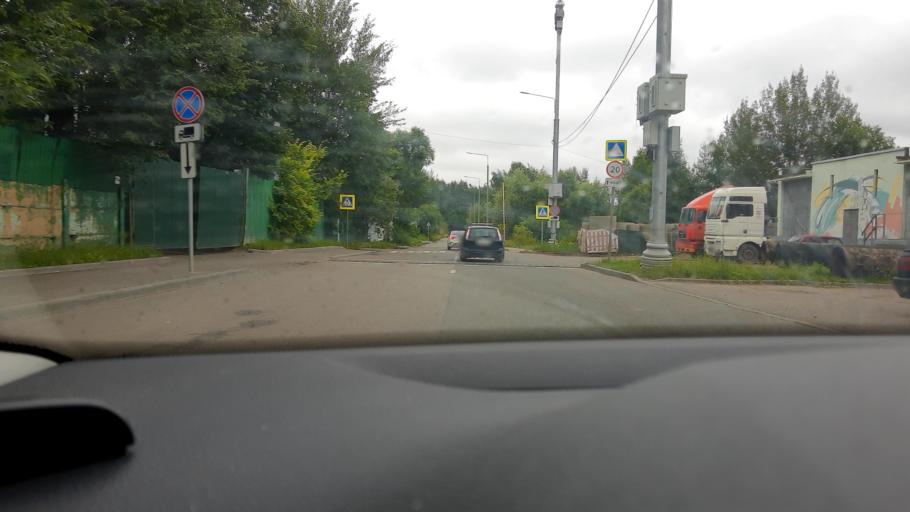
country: RU
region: Moscow
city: Khimki
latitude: 55.8837
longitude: 37.3910
